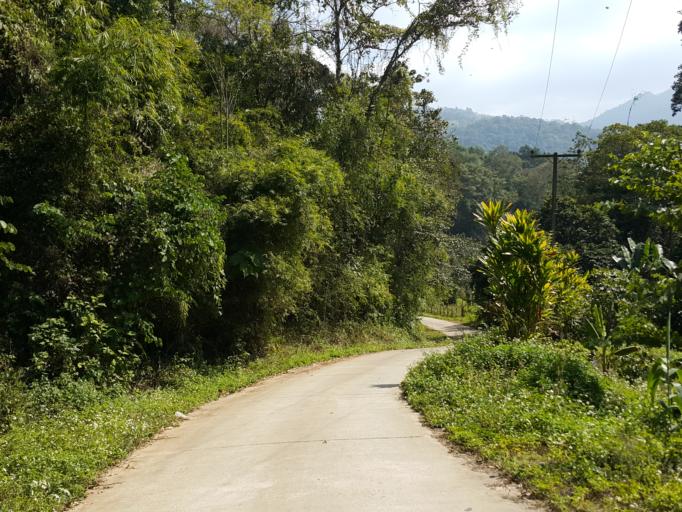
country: TH
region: Lampang
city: Wang Nuea
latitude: 19.0638
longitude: 99.3603
